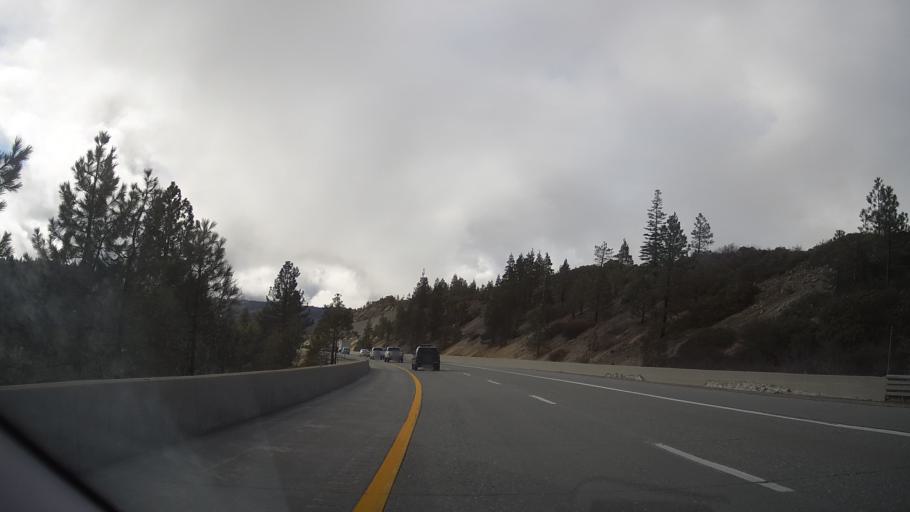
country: US
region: California
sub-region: Sierra County
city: Downieville
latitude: 39.3103
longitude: -120.6391
